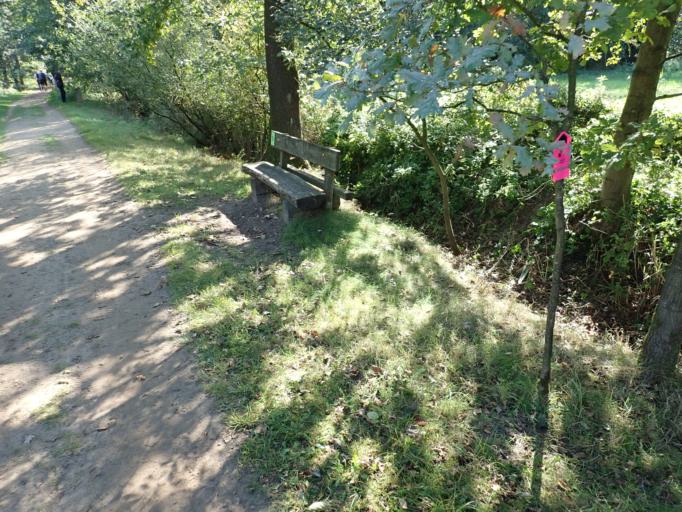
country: BE
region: Flanders
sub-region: Provincie Oost-Vlaanderen
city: Sint-Gillis-Waas
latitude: 51.2424
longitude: 4.0837
